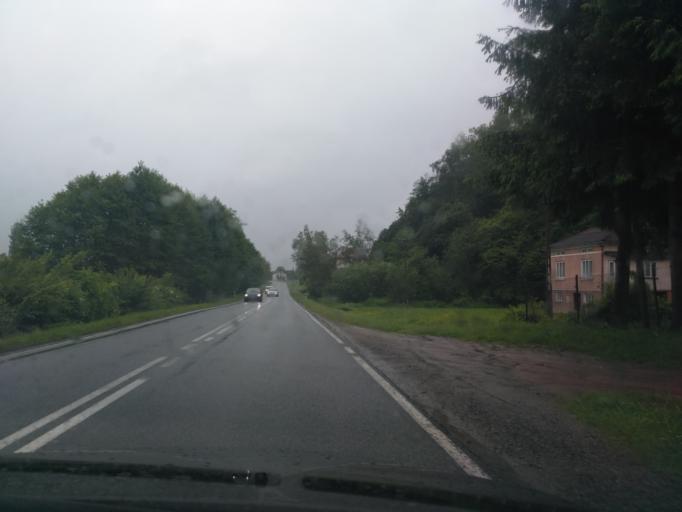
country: PL
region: Subcarpathian Voivodeship
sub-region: Powiat krosnienski
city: Leki
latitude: 49.8042
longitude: 21.6400
